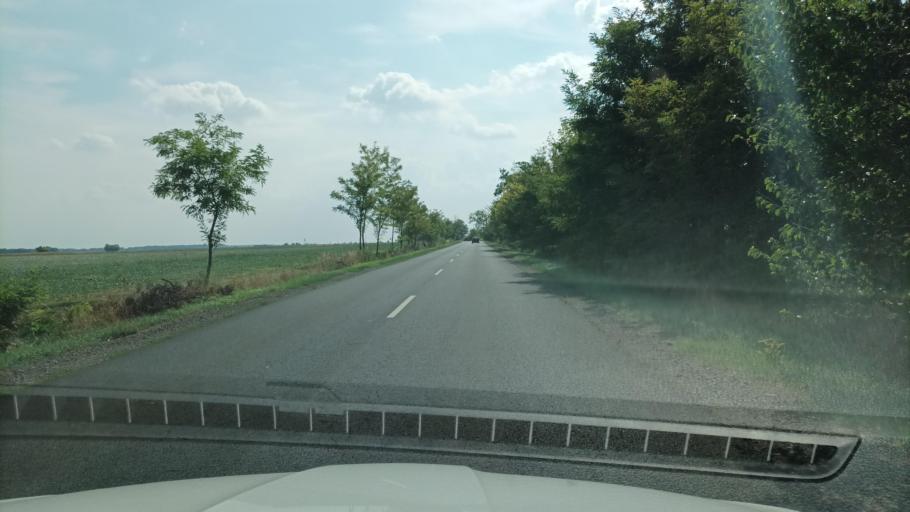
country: HU
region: Pest
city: Zsambok
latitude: 47.5749
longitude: 19.6013
